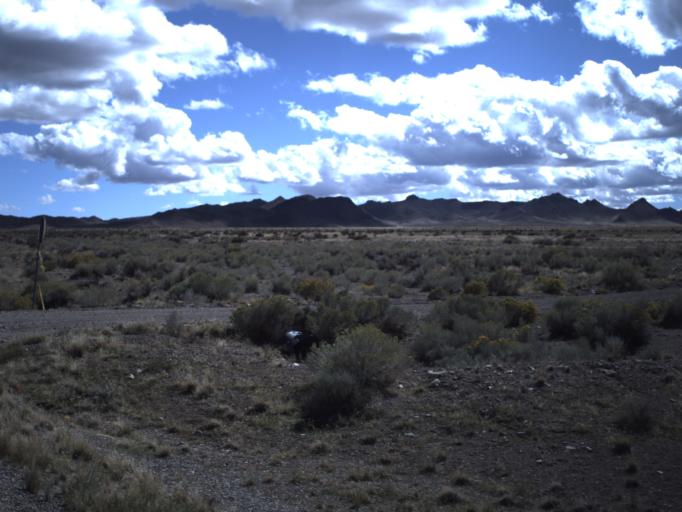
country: US
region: Utah
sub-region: Beaver County
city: Milford
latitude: 38.4495
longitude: -113.3426
